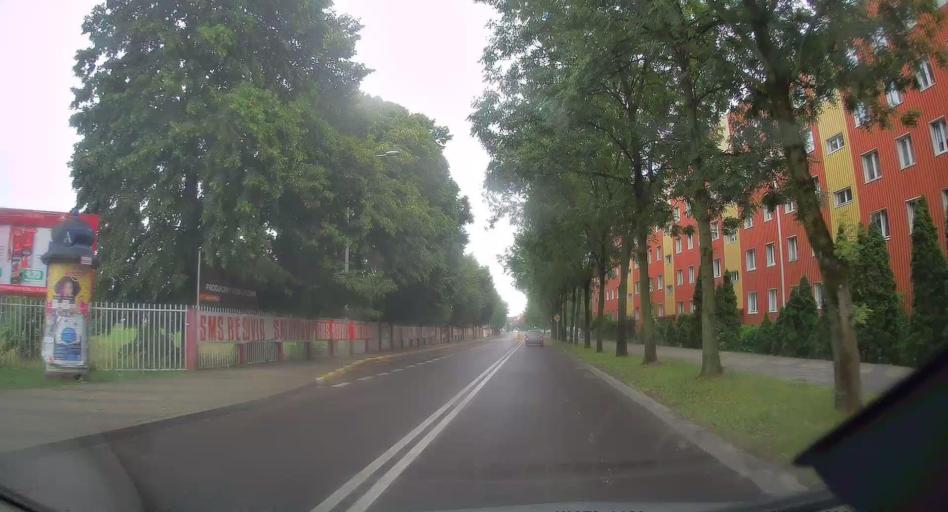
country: PL
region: Subcarpathian Voivodeship
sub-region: Rzeszow
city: Rzeszow
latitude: 50.0394
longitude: 21.9820
